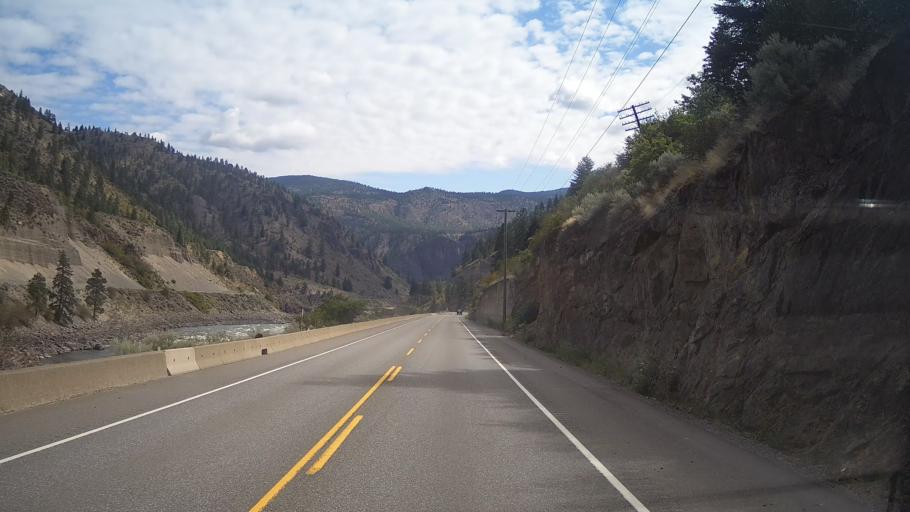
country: CA
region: British Columbia
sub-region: Thompson-Nicola Regional District
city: Ashcroft
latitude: 50.2595
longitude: -121.4280
